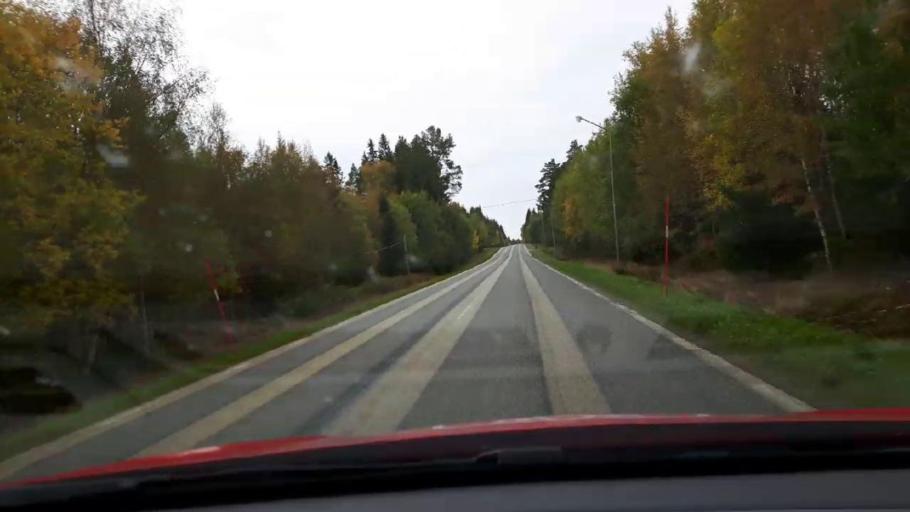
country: SE
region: Jaemtland
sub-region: Bergs Kommun
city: Hoverberg
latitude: 62.8953
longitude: 14.3481
